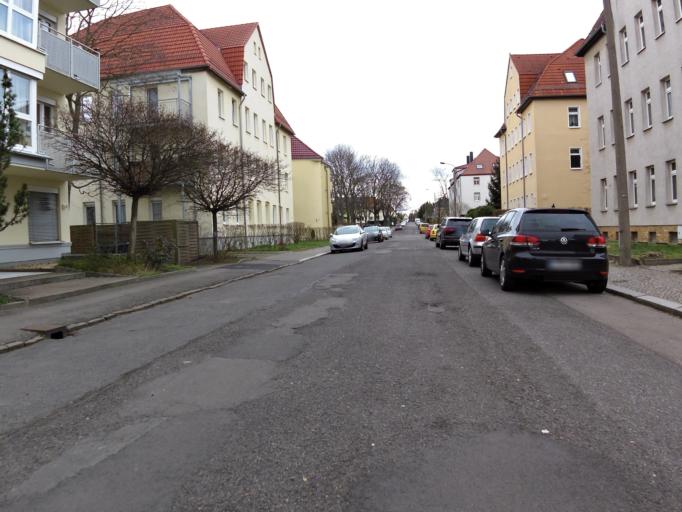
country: DE
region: Saxony
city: Markkleeberg
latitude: 51.2847
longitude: 12.4028
